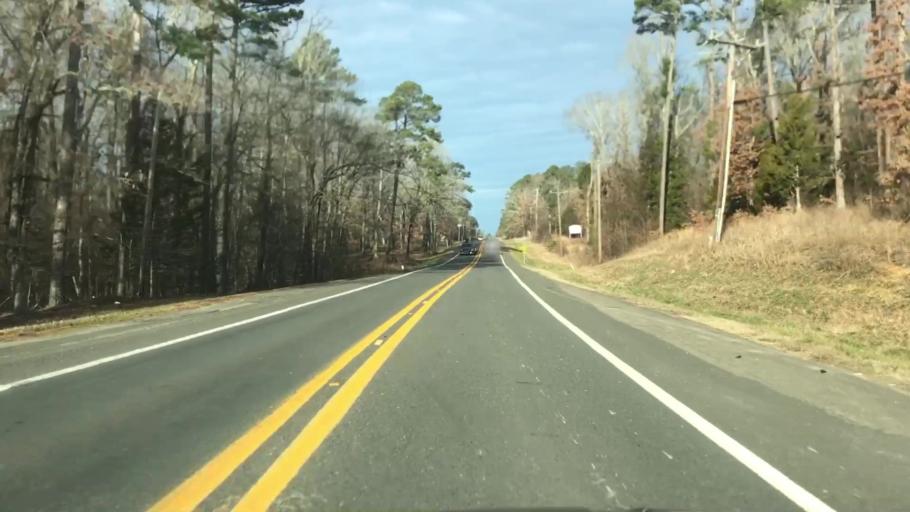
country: US
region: Arkansas
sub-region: Montgomery County
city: Mount Ida
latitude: 34.5395
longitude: -93.6040
